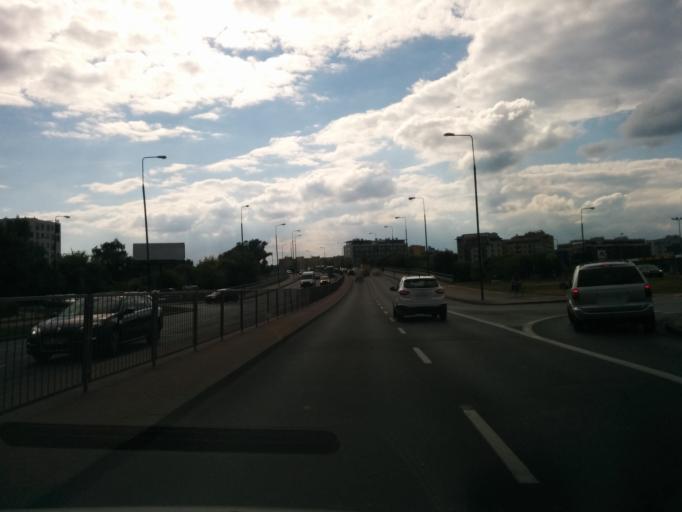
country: PL
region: Masovian Voivodeship
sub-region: Warszawa
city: Bemowo
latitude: 52.2405
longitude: 20.9299
